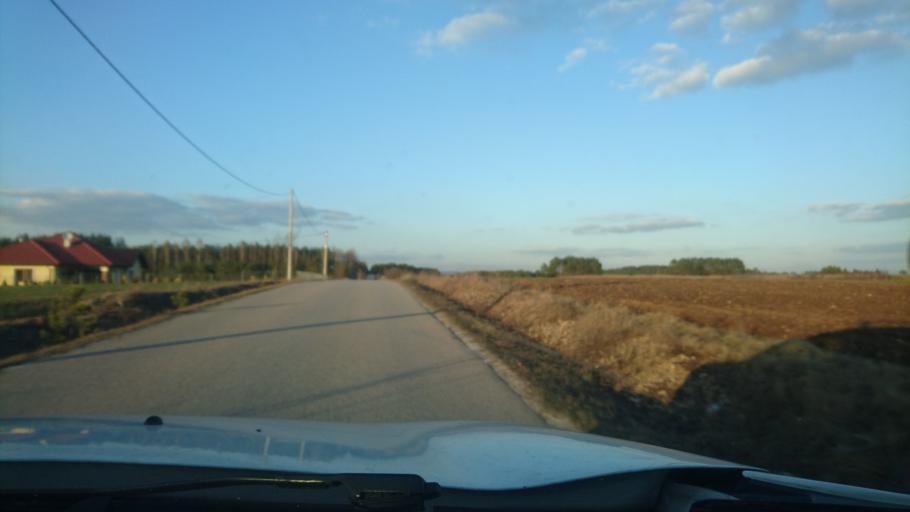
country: PL
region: Swietokrzyskie
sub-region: Powiat kielecki
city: Morawica
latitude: 50.7681
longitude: 20.6916
